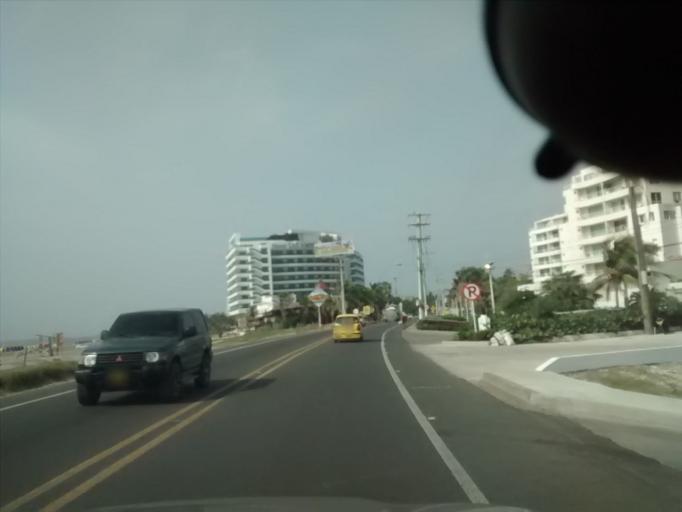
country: CO
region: Bolivar
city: Cartagena
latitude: 10.4572
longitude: -75.5096
